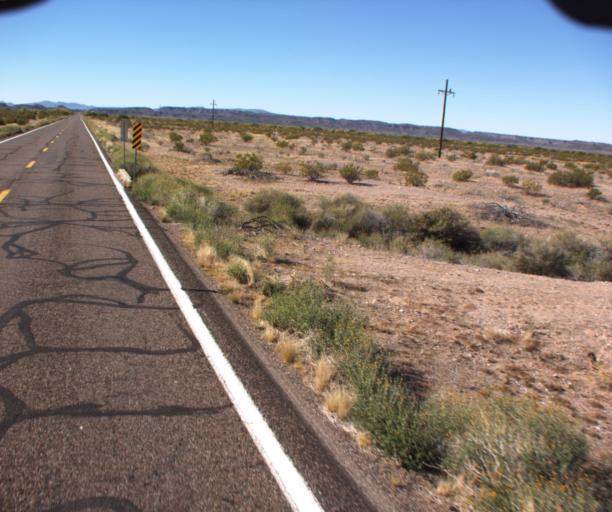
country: US
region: Arizona
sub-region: Pima County
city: Ajo
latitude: 32.6230
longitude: -112.8663
